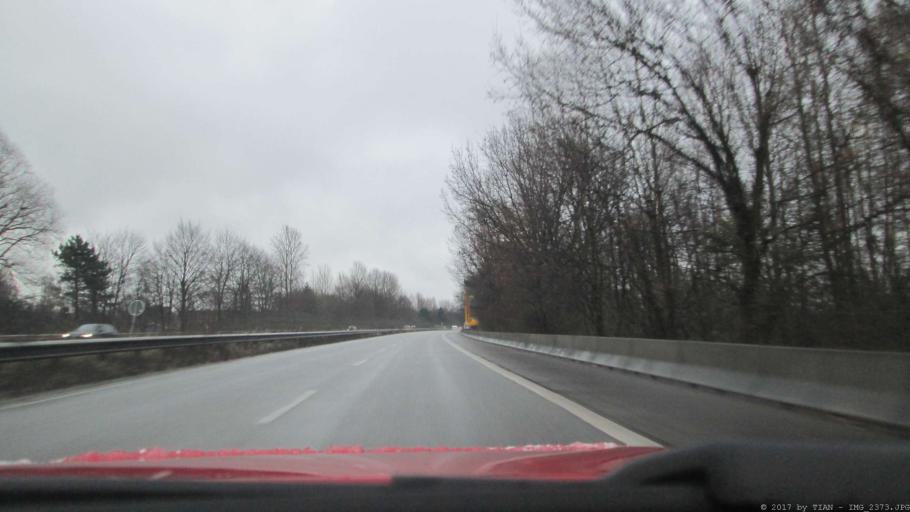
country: DE
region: Hamburg
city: Marienthal
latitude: 53.5493
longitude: 10.0715
